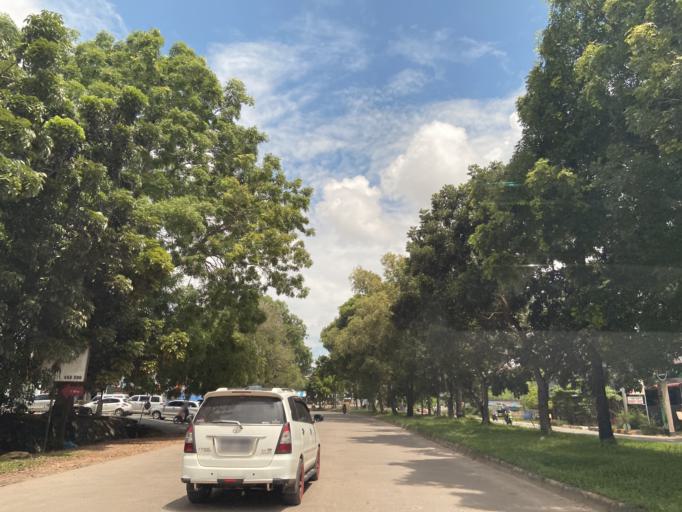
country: SG
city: Singapore
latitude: 1.1404
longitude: 104.0013
